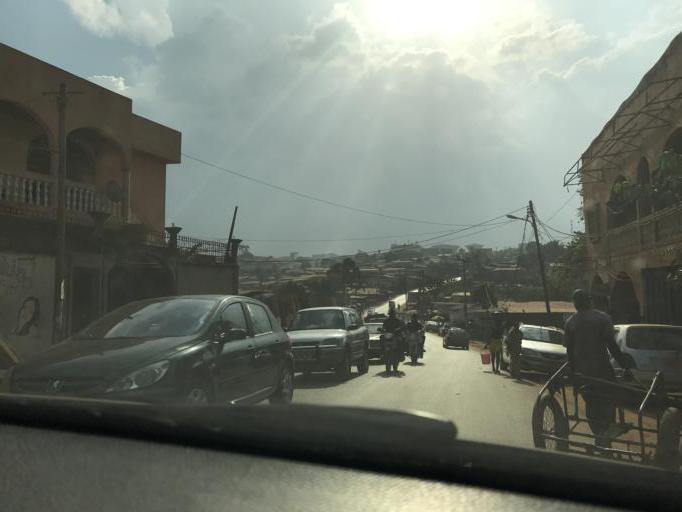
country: CM
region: Centre
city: Yaounde
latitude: 3.8853
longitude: 11.5301
